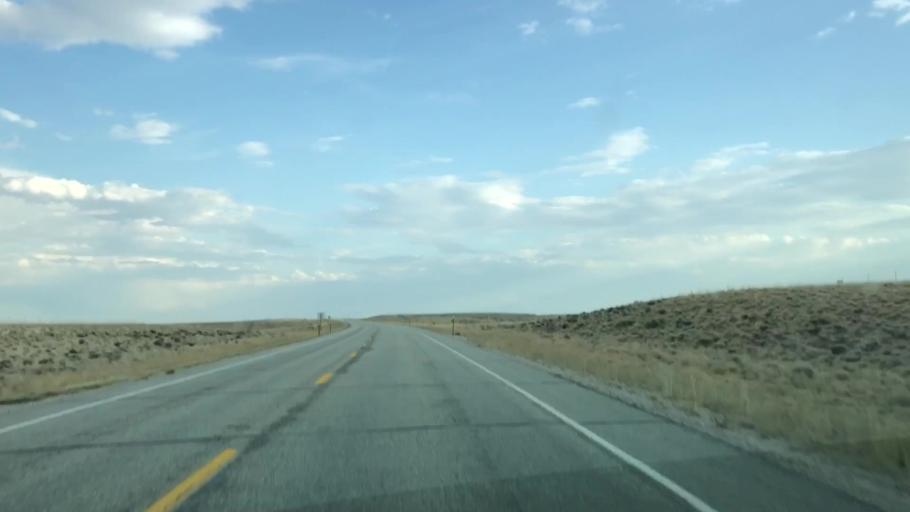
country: US
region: Wyoming
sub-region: Sweetwater County
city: North Rock Springs
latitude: 42.2819
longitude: -109.4863
